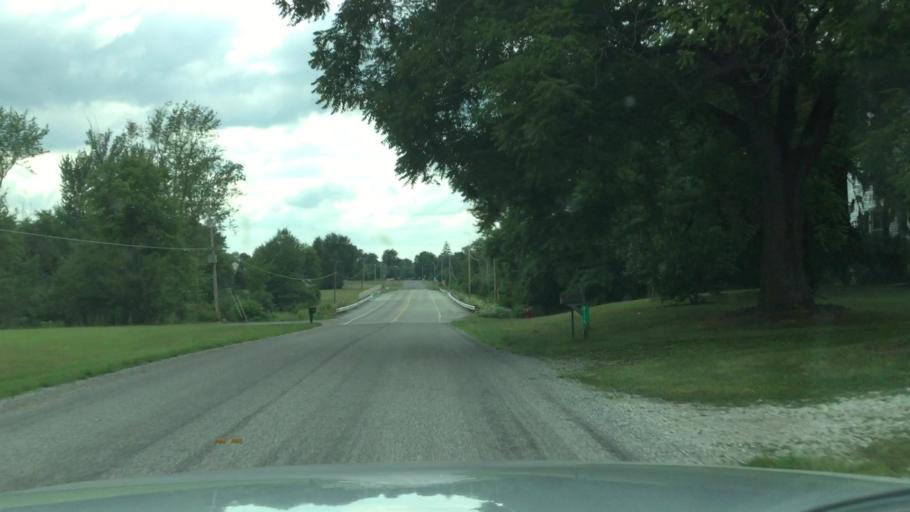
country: US
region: Michigan
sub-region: Saginaw County
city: Frankenmuth
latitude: 43.3218
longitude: -83.7920
